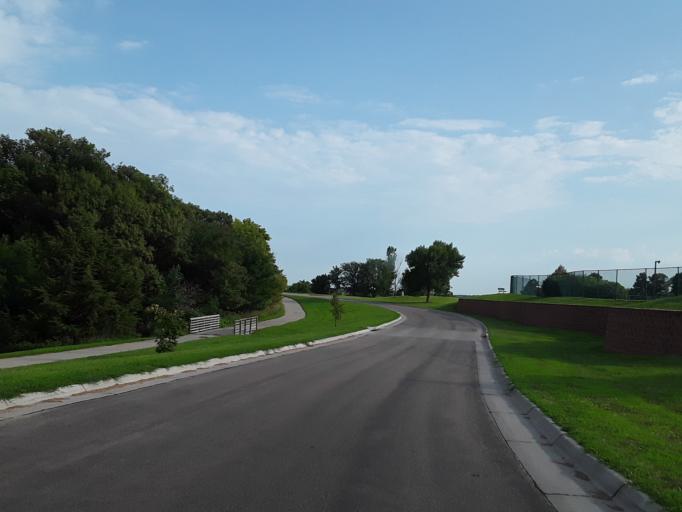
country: US
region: Nebraska
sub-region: Saunders County
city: Ashland
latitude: 41.0268
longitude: -96.3095
